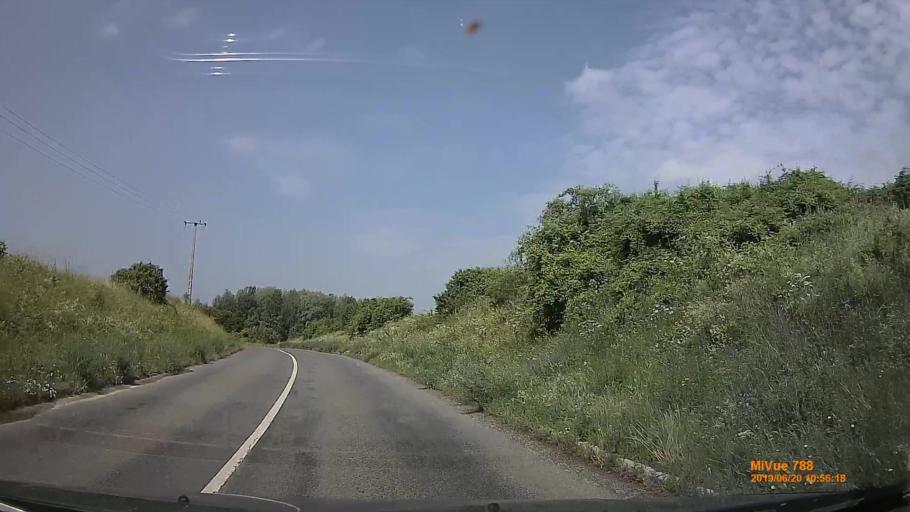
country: HU
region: Baranya
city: Mecseknadasd
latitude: 46.1565
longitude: 18.5380
